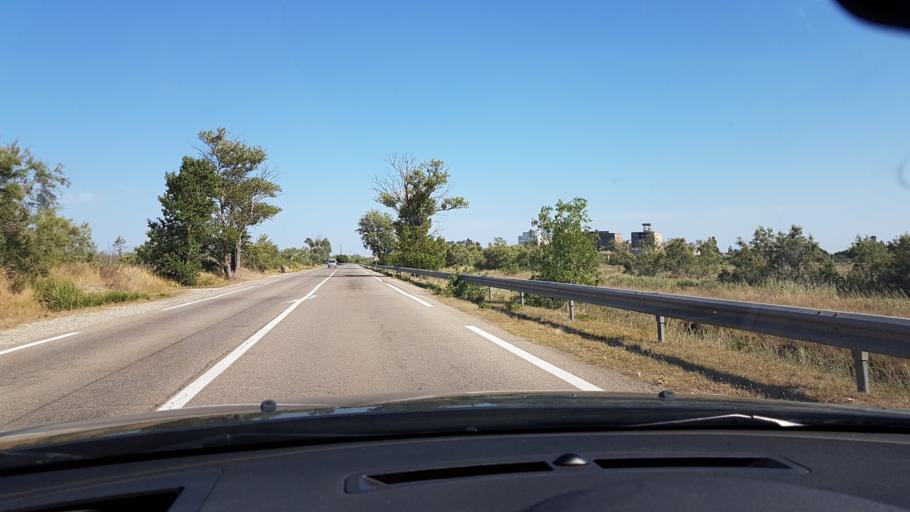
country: FR
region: Provence-Alpes-Cote d'Azur
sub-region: Departement des Bouches-du-Rhone
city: Port-Saint-Louis-du-Rhone
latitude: 43.3929
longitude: 4.8168
